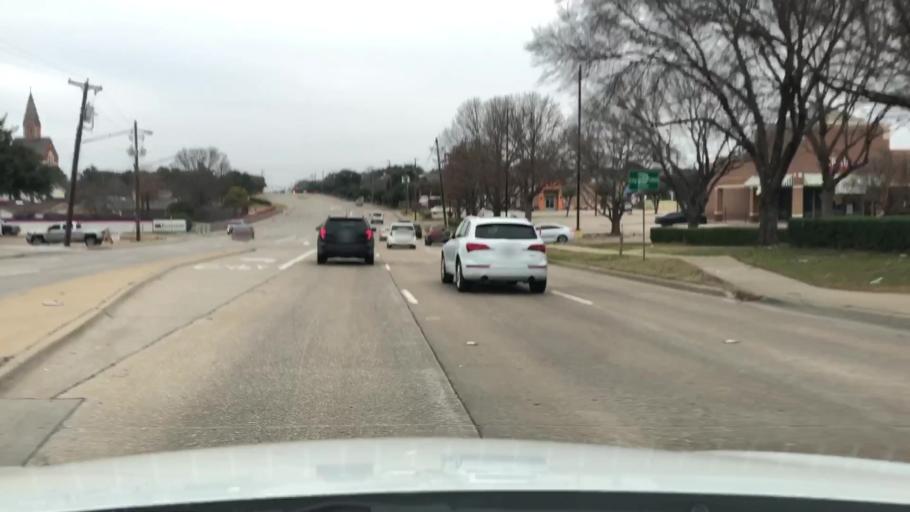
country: US
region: Texas
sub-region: Dallas County
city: Addison
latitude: 32.9877
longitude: -96.8547
